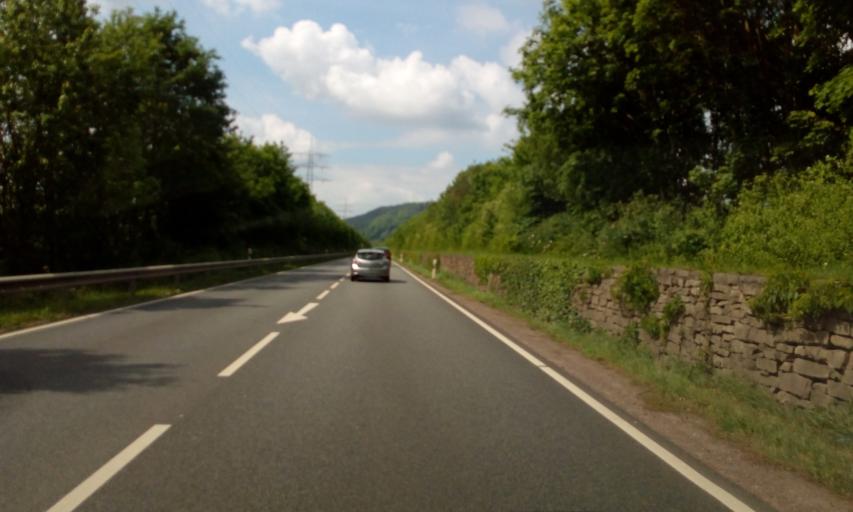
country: DE
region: Rheinland-Pfalz
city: Kenn
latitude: 49.8141
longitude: 6.7012
